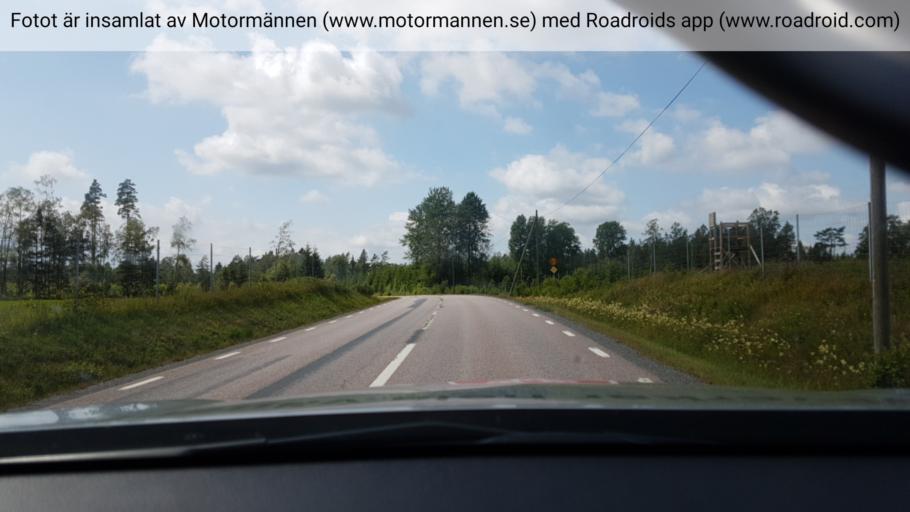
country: SE
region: Vaestra Goetaland
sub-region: Marks Kommun
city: Fritsla
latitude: 57.4939
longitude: 12.8611
